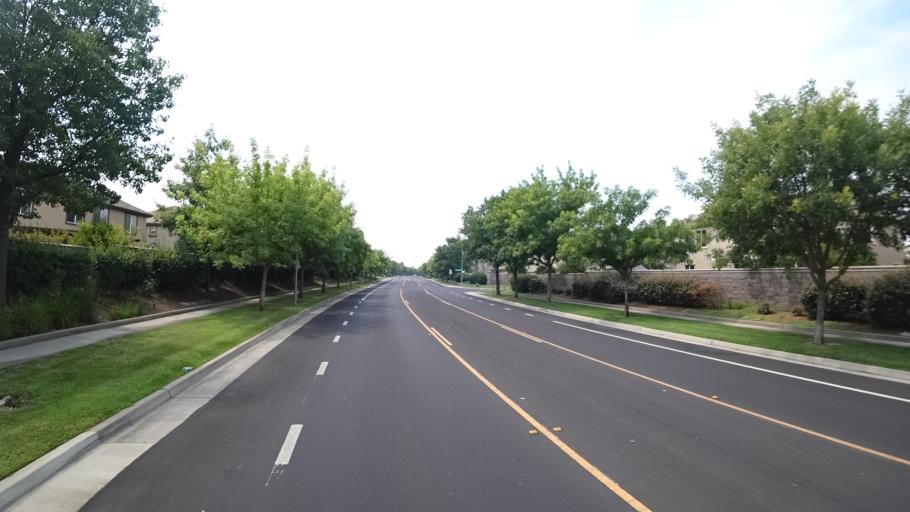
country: US
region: California
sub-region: Sacramento County
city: Laguna
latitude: 38.3830
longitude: -121.4257
